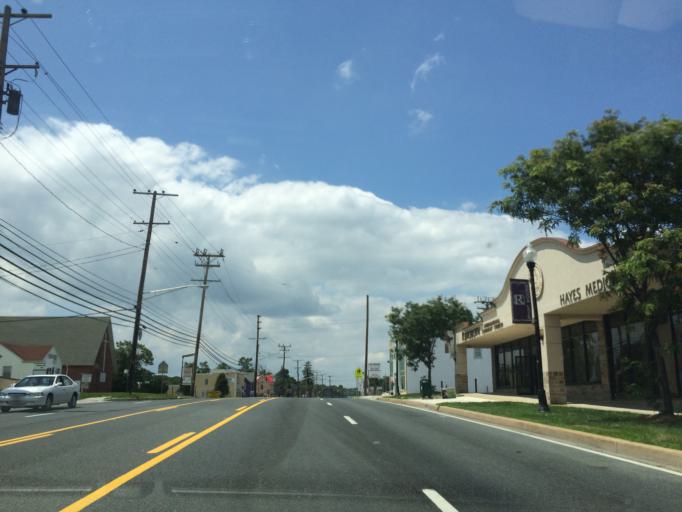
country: US
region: Maryland
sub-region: Baltimore County
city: Randallstown
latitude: 39.3676
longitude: -76.7959
